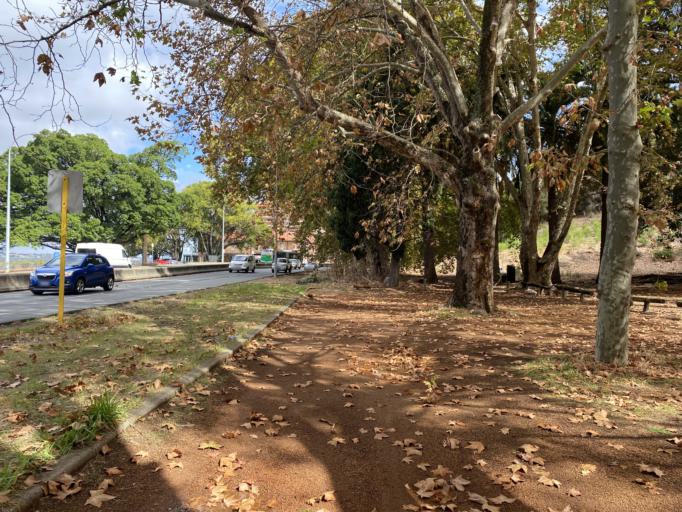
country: AU
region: Western Australia
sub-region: City of Perth
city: West Perth
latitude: -31.9634
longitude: 115.8419
